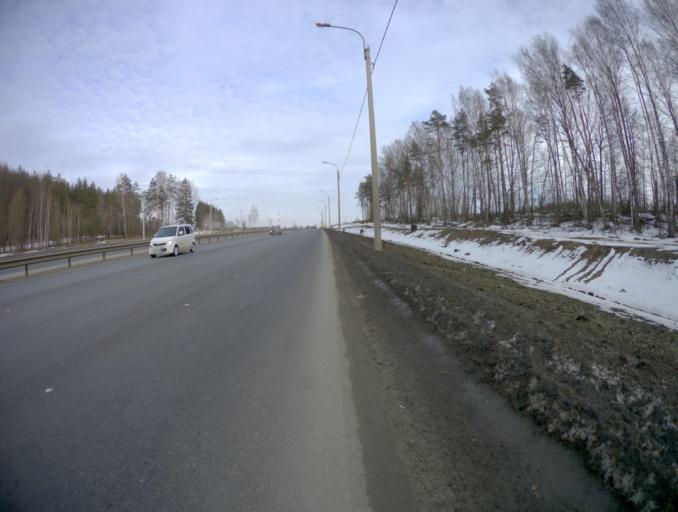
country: RU
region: Vladimir
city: Kommunar
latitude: 56.0739
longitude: 40.4856
